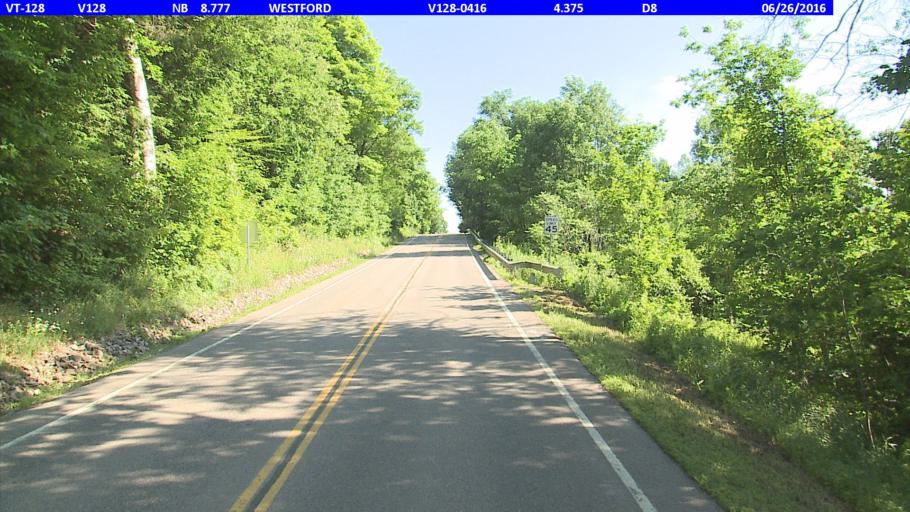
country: US
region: Vermont
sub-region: Chittenden County
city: Milton
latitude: 44.6174
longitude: -73.0156
